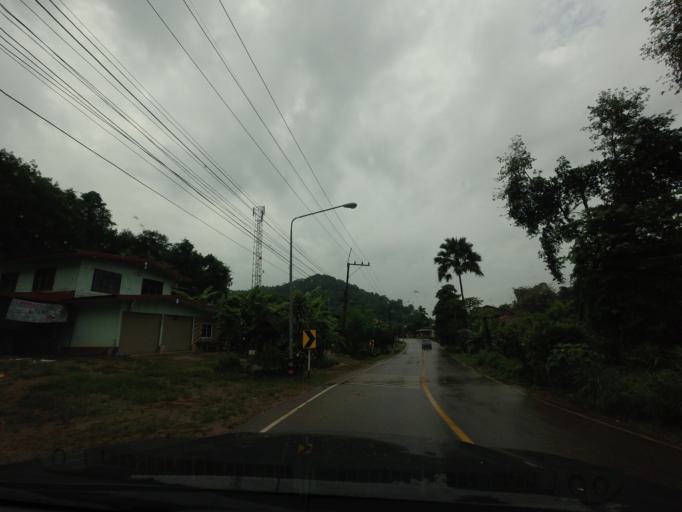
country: TH
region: Nong Khai
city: Sangkhom
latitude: 18.2074
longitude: 102.1310
